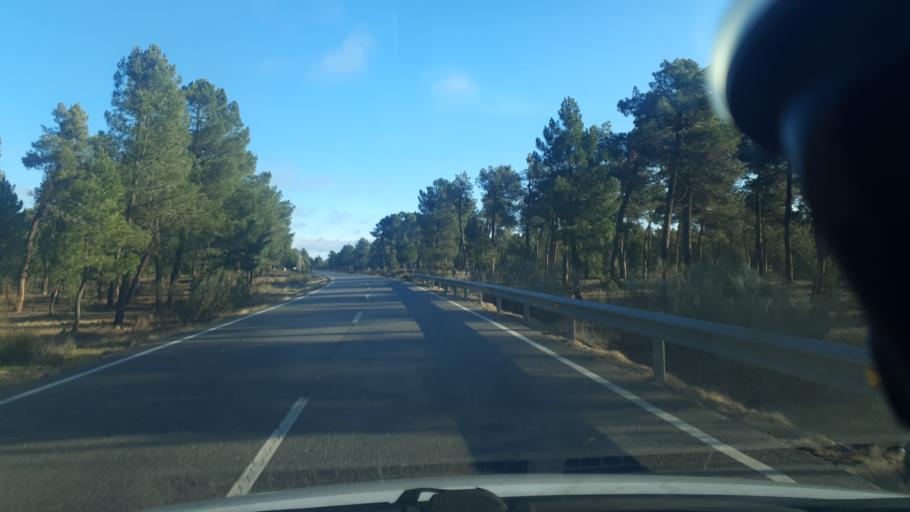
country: ES
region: Castille and Leon
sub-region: Provincia de Avila
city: Tinosillos
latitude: 40.9467
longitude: -4.7169
